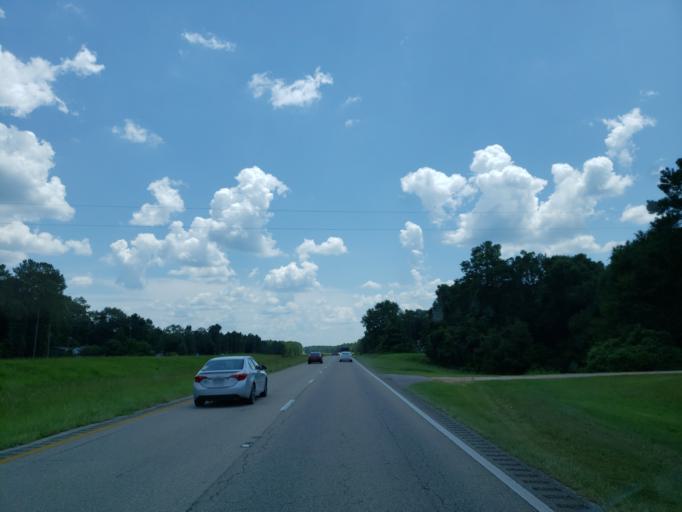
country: US
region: Mississippi
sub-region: Wayne County
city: Belmont
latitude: 31.4980
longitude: -88.4947
